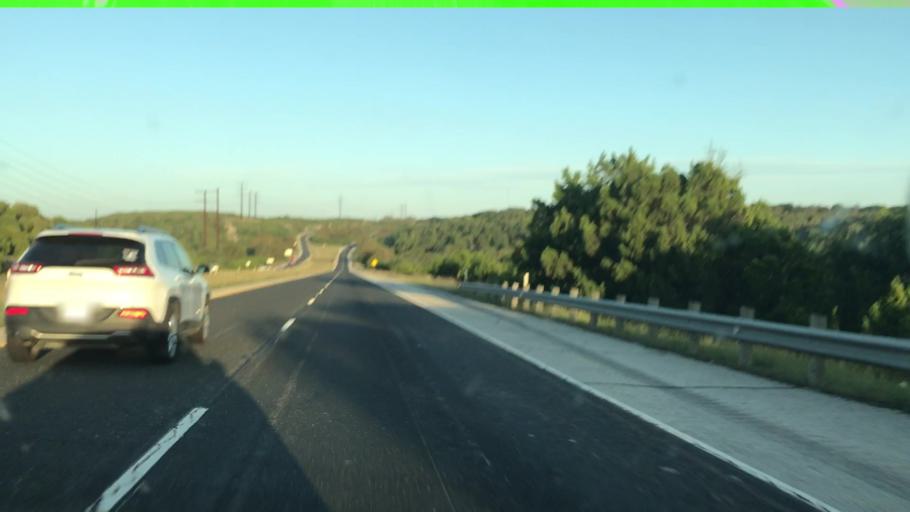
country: US
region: Texas
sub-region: Kerr County
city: Kerrville
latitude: 30.0695
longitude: -99.0934
